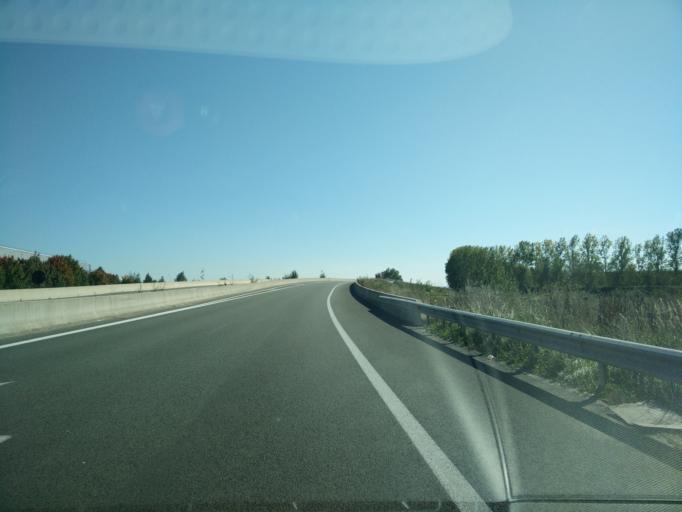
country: FR
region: Ile-de-France
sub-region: Departement de Seine-et-Marne
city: Mitry-Mory
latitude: 48.9936
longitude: 2.6532
